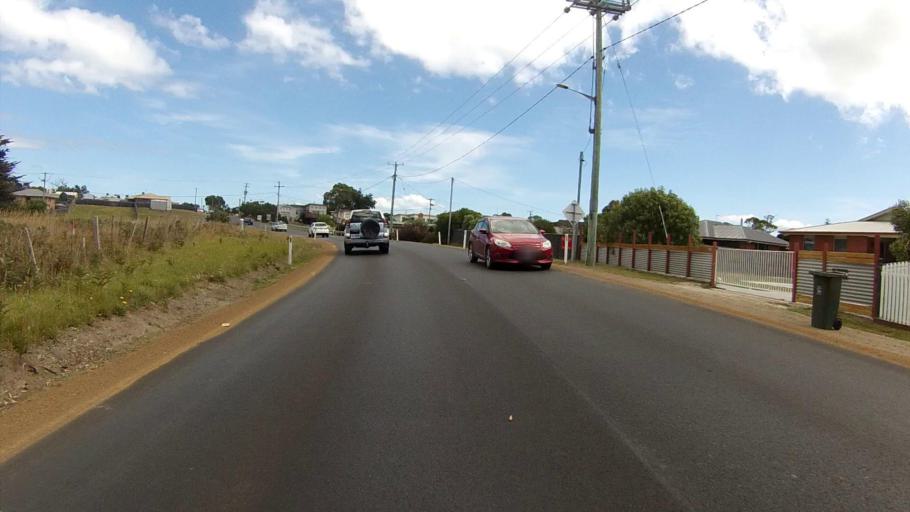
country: AU
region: Tasmania
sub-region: Sorell
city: Sorell
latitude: -42.8507
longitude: 147.6235
